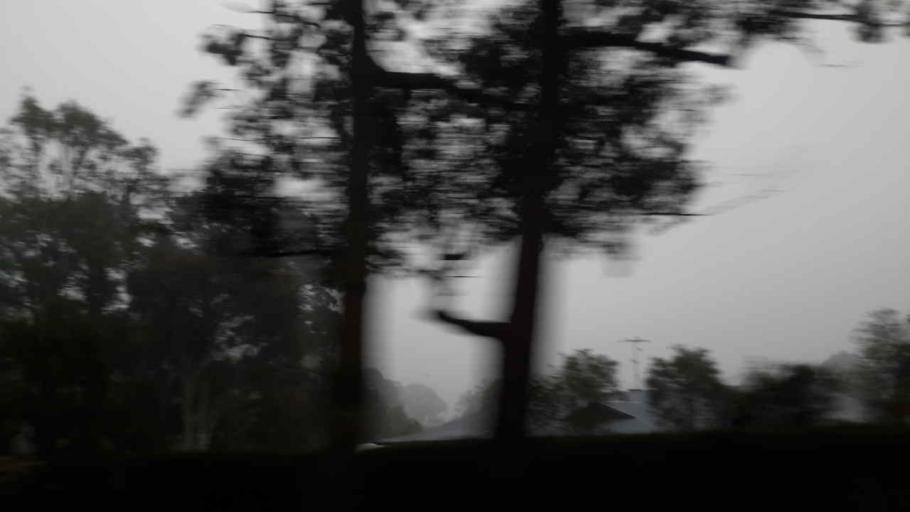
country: AU
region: New South Wales
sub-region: Wollondilly
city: Douglas Park
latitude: -34.2376
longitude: 150.7283
